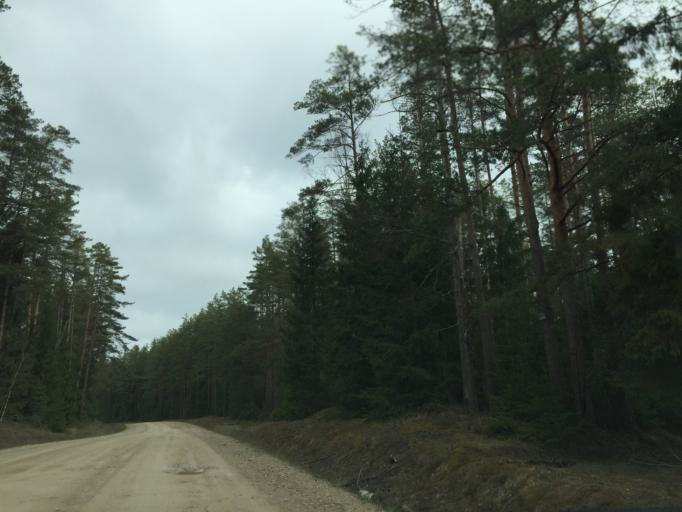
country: EE
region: Valgamaa
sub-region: Valga linn
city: Valga
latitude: 57.5902
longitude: 26.2202
